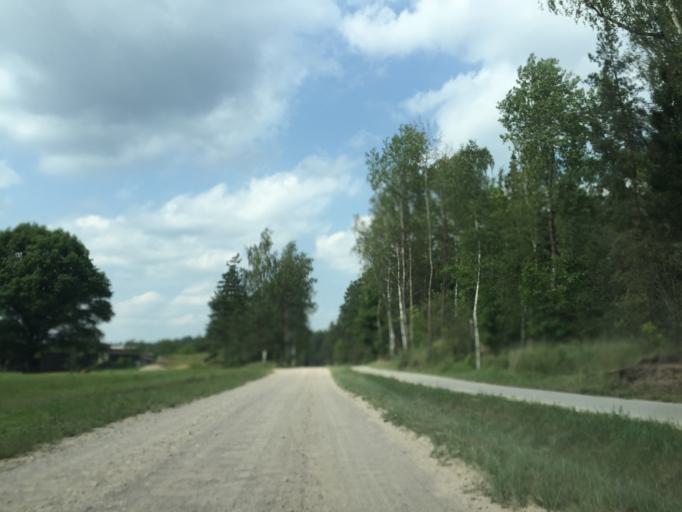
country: LV
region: Olaine
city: Olaine
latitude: 56.7771
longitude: 23.9024
